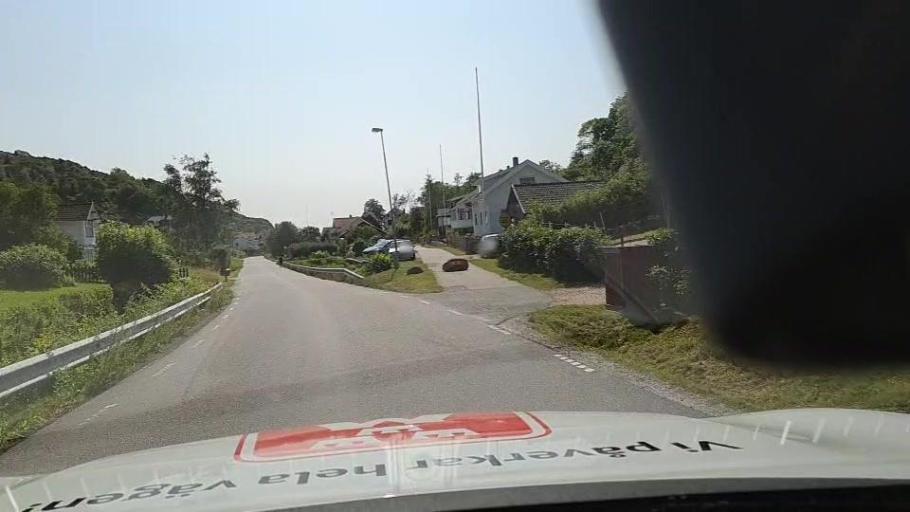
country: SE
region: Vaestra Goetaland
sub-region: Tjorns Kommun
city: Skaerhamn
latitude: 58.1085
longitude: 11.5175
